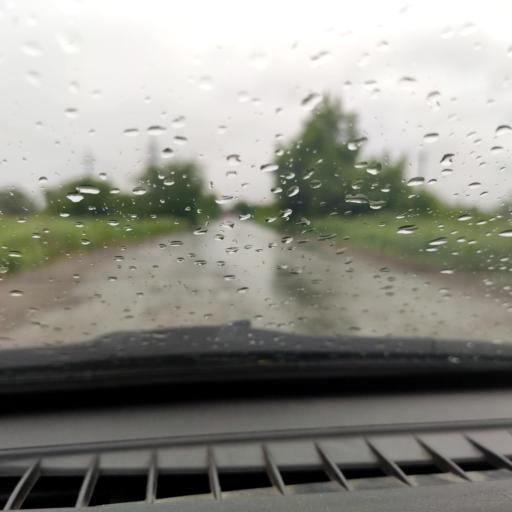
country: RU
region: Samara
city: Tol'yatti
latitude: 53.5662
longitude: 49.3562
